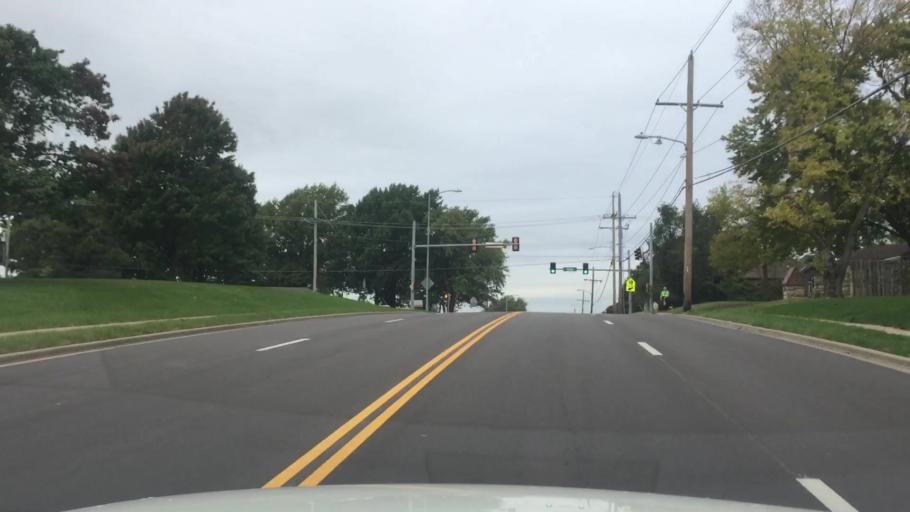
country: US
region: Kansas
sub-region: Johnson County
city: Shawnee
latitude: 39.0220
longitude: -94.7556
